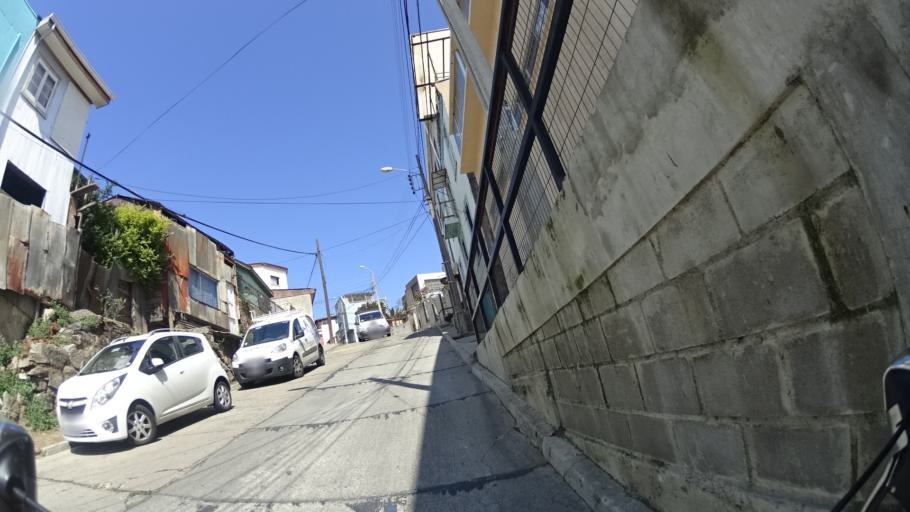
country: CL
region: Valparaiso
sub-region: Provincia de Valparaiso
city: Valparaiso
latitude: -33.0508
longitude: -71.6218
